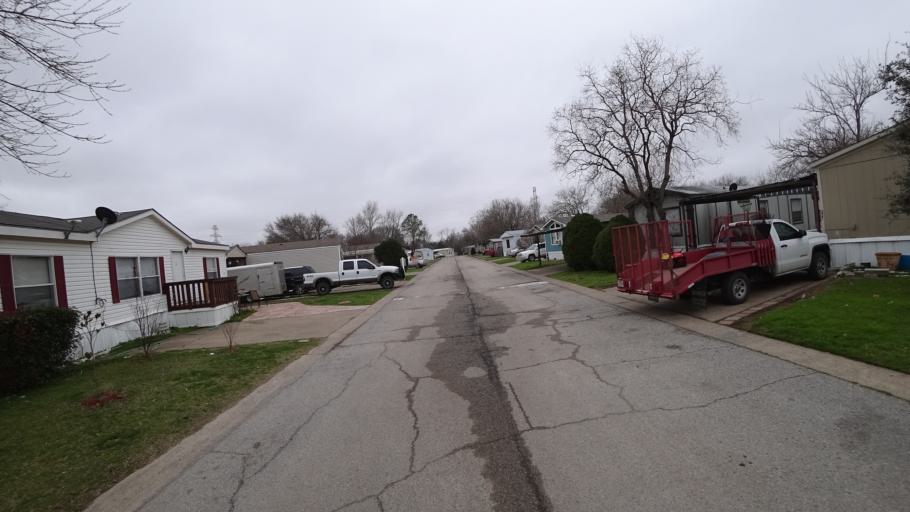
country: US
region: Texas
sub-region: Denton County
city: Lewisville
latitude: 33.0606
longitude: -96.9953
